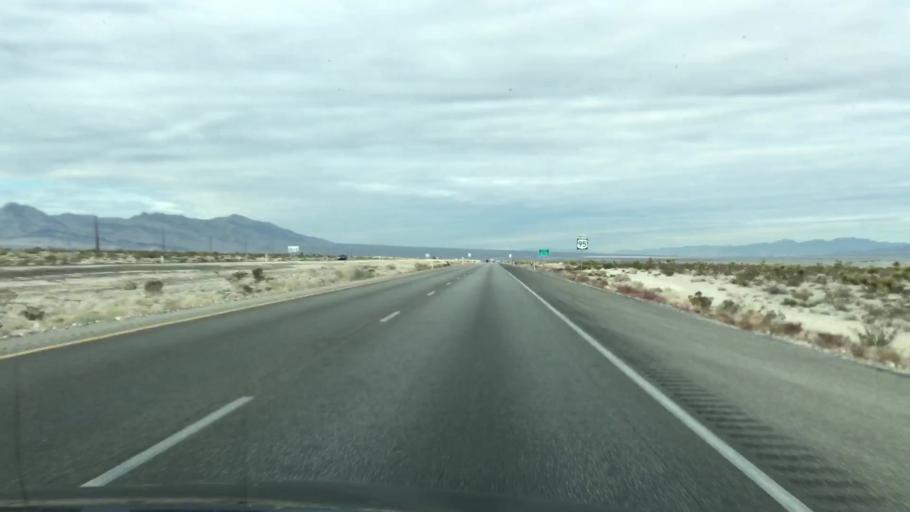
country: US
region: Nevada
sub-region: Clark County
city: Summerlin South
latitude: 36.3673
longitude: -115.3573
